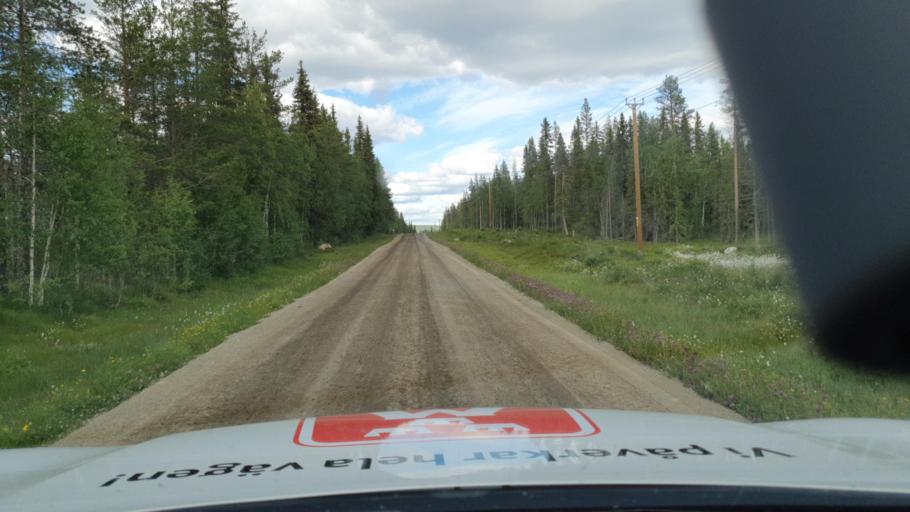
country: SE
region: Vaesterbotten
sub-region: Lycksele Kommun
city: Lycksele
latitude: 64.3127
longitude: 18.3010
